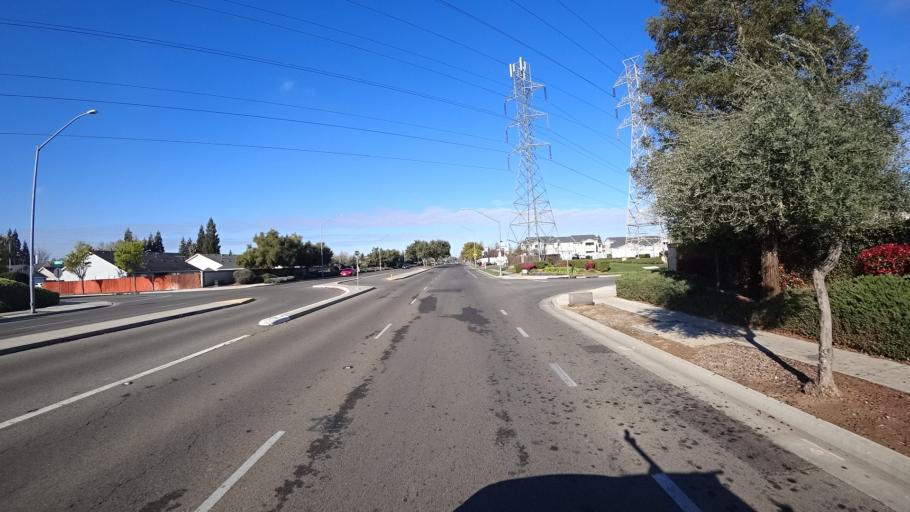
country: US
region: California
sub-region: Fresno County
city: West Park
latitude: 36.8219
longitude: -119.8803
